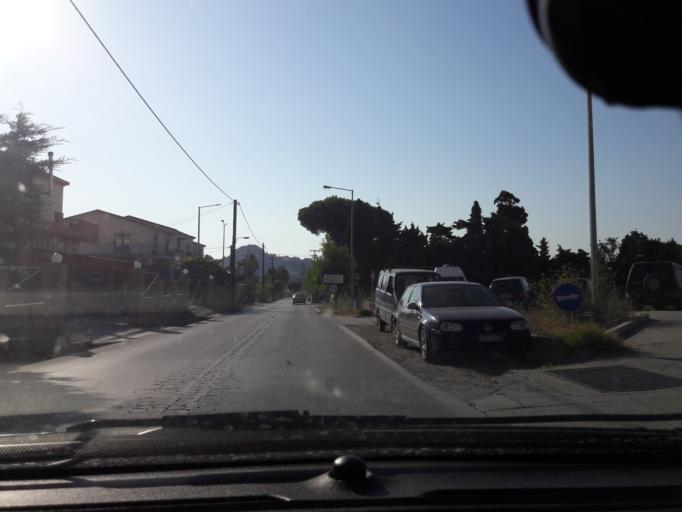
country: GR
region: North Aegean
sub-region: Nomos Lesvou
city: Myrina
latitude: 39.8704
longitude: 25.0697
